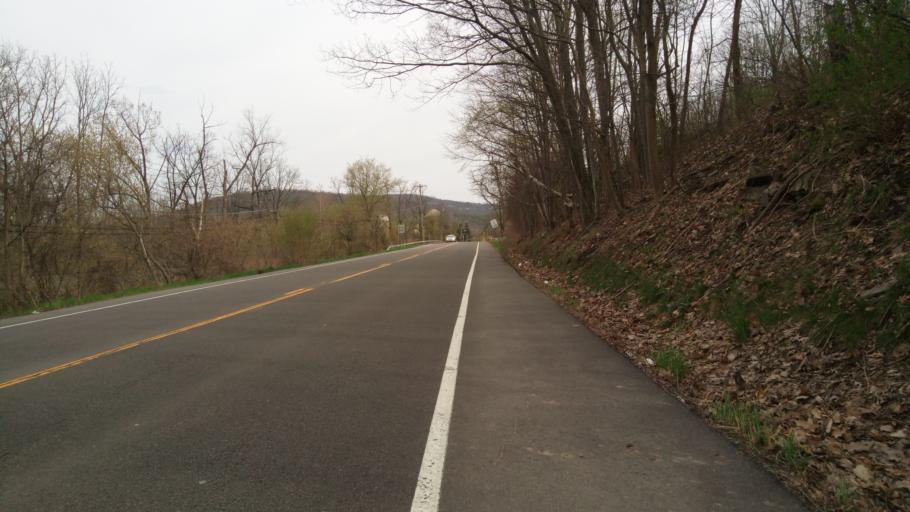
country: US
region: New York
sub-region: Chemung County
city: Southport
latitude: 42.0200
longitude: -76.7361
